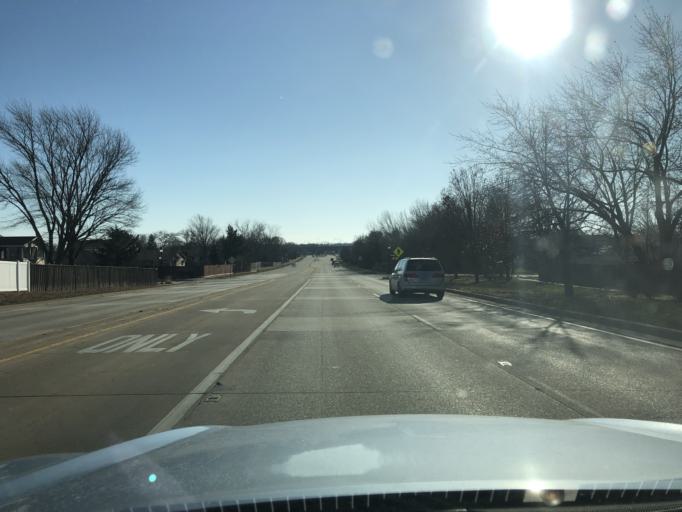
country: US
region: Illinois
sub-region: DuPage County
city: Roselle
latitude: 41.9982
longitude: -88.0460
